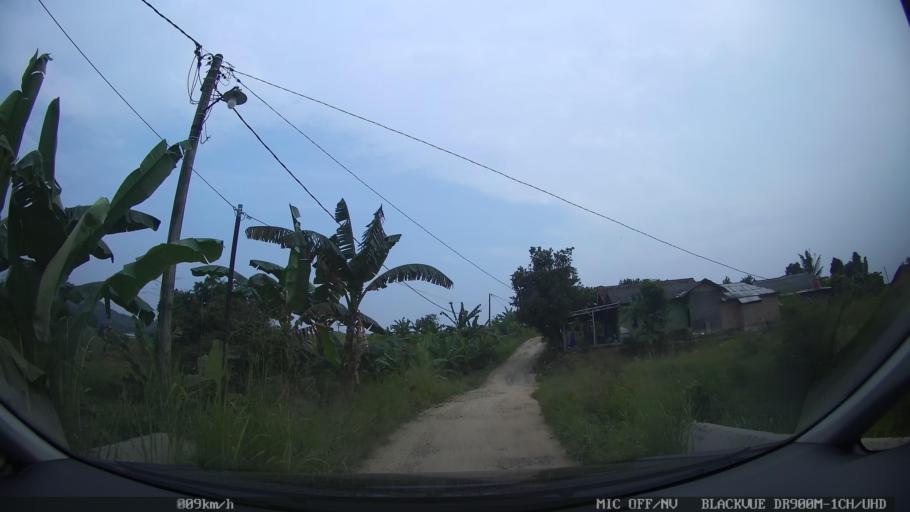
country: ID
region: Lampung
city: Panjang
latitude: -5.4236
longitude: 105.3454
